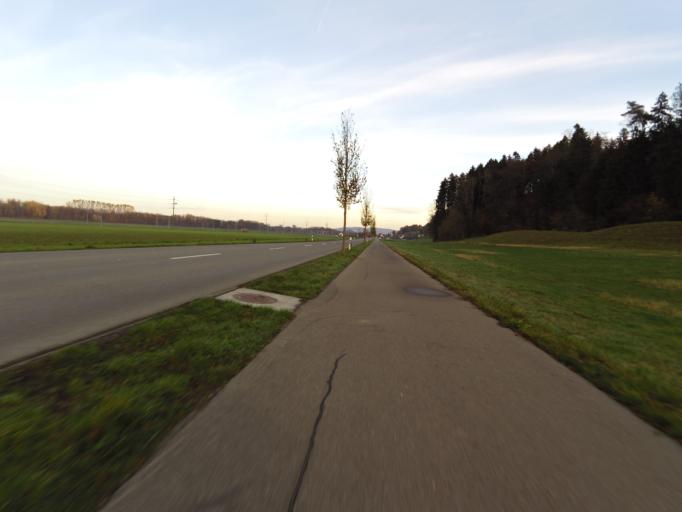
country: CH
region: Thurgau
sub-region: Frauenfeld District
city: Mullheim
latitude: 47.5801
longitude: 8.9924
